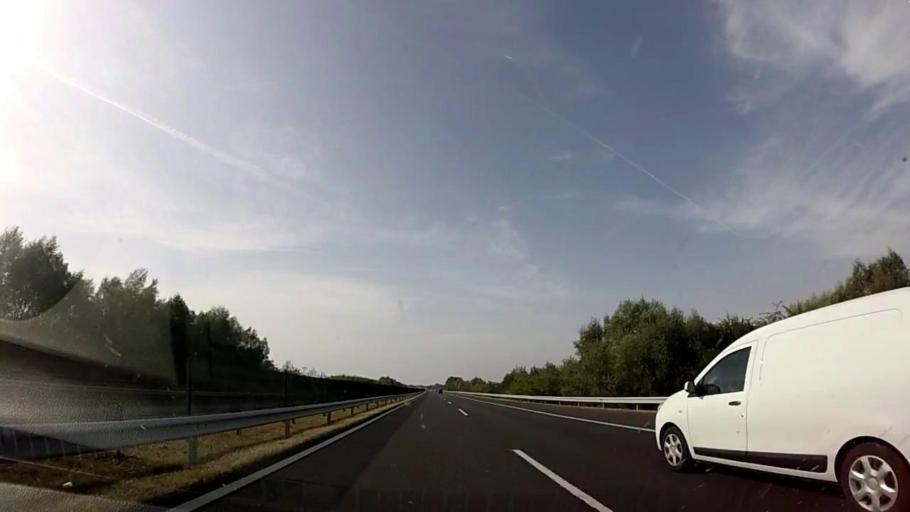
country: HU
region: Zala
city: Zalakomar
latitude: 46.5622
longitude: 17.2319
